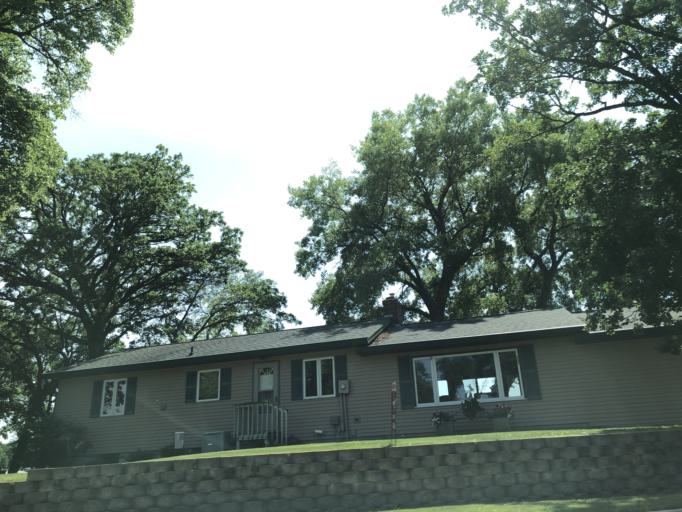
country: US
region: Minnesota
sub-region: Douglas County
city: Alexandria
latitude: 45.9314
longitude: -95.3783
